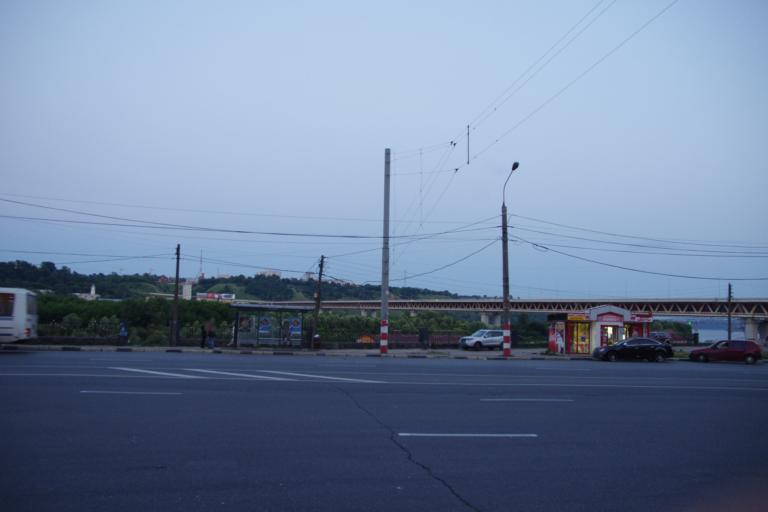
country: RU
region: Nizjnij Novgorod
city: Nizhniy Novgorod
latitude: 56.3245
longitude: 43.9584
